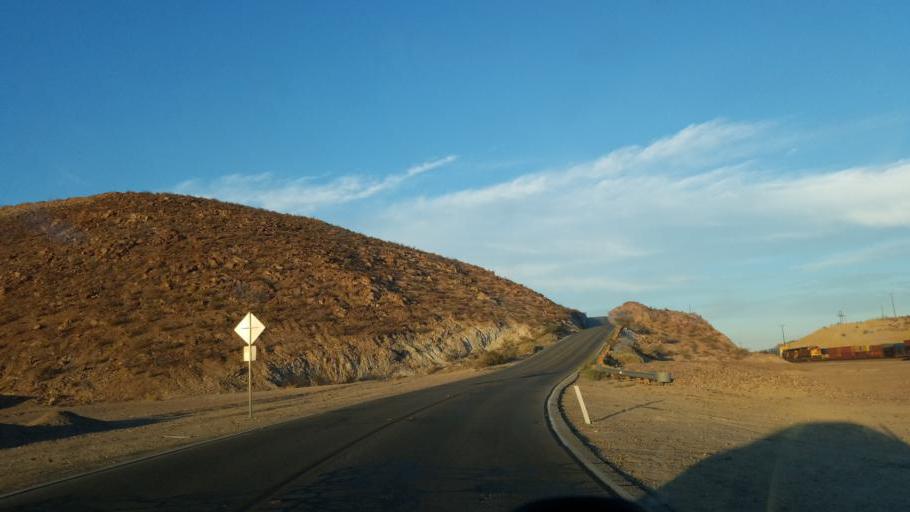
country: US
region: California
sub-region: San Bernardino County
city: Barstow
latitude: 34.9036
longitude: -117.0137
